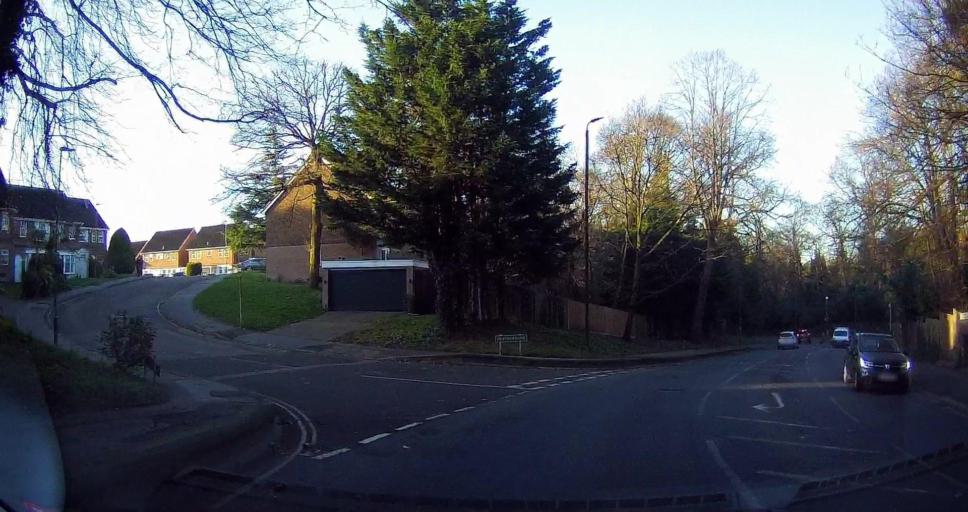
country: GB
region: England
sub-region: Greater London
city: Chislehurst
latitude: 51.4065
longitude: 0.0617
